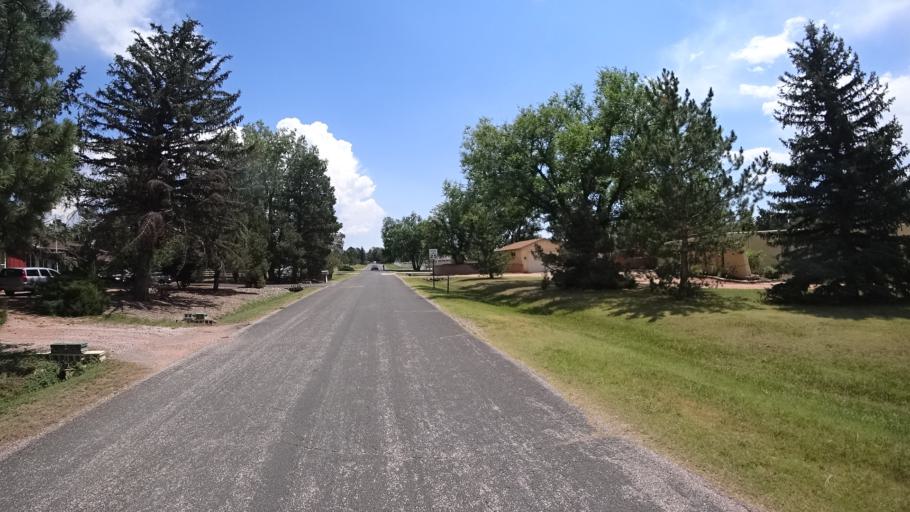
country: US
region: Colorado
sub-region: El Paso County
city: Air Force Academy
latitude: 38.9382
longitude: -104.8104
